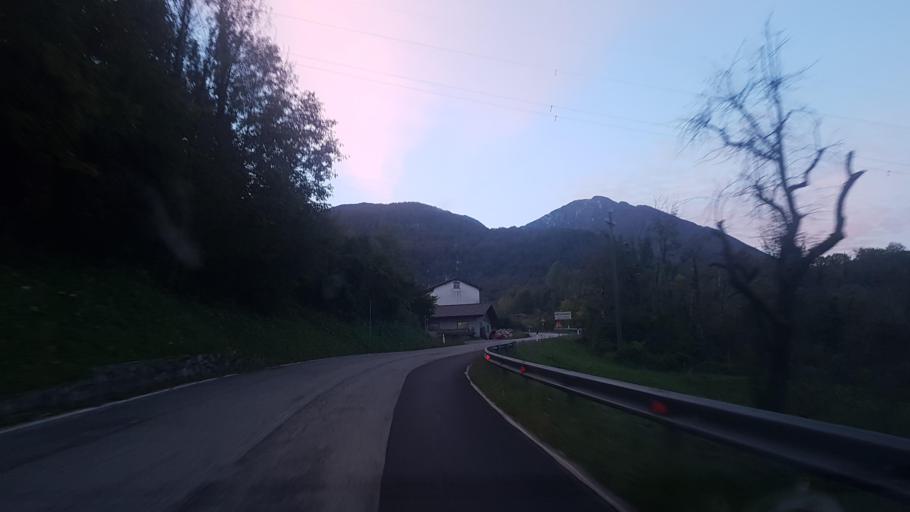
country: IT
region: Friuli Venezia Giulia
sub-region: Provincia di Udine
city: Chiaulis
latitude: 46.3859
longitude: 12.9929
